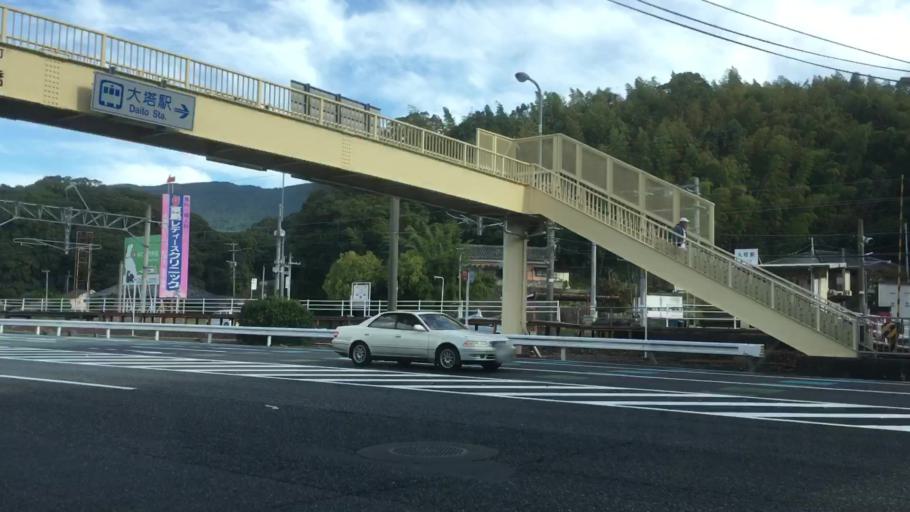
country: JP
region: Nagasaki
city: Sasebo
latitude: 33.1487
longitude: 129.7819
